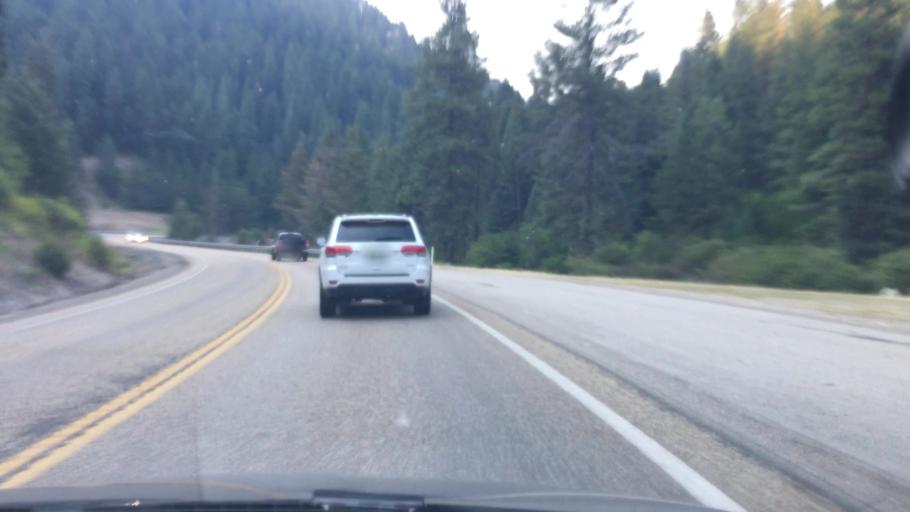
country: US
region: Idaho
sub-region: Valley County
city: Cascade
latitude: 44.1947
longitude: -116.1122
